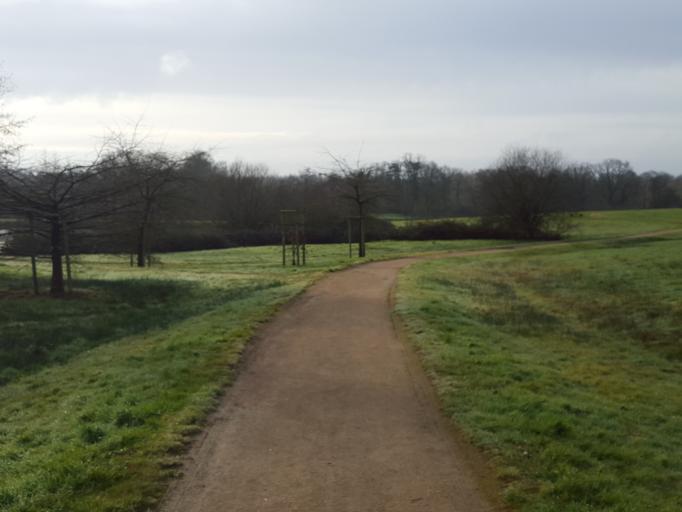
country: FR
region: Pays de la Loire
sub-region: Departement de la Vendee
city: Mouilleron-le-Captif
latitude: 46.7131
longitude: -1.4397
